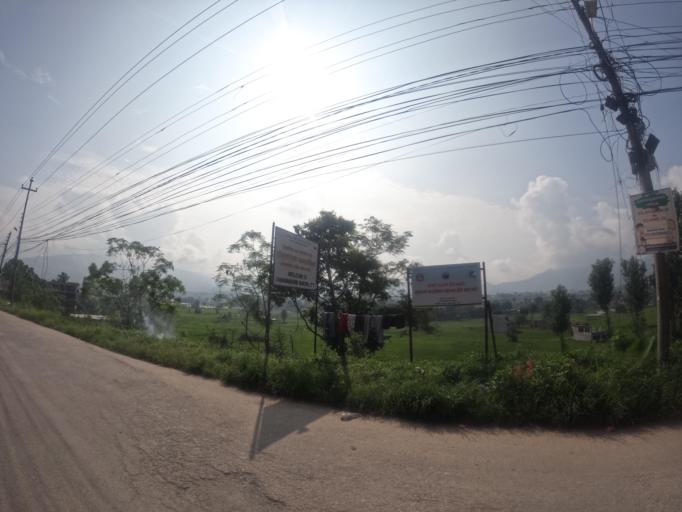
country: NP
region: Central Region
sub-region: Bagmati Zone
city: Bhaktapur
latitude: 27.6805
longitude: 85.4464
